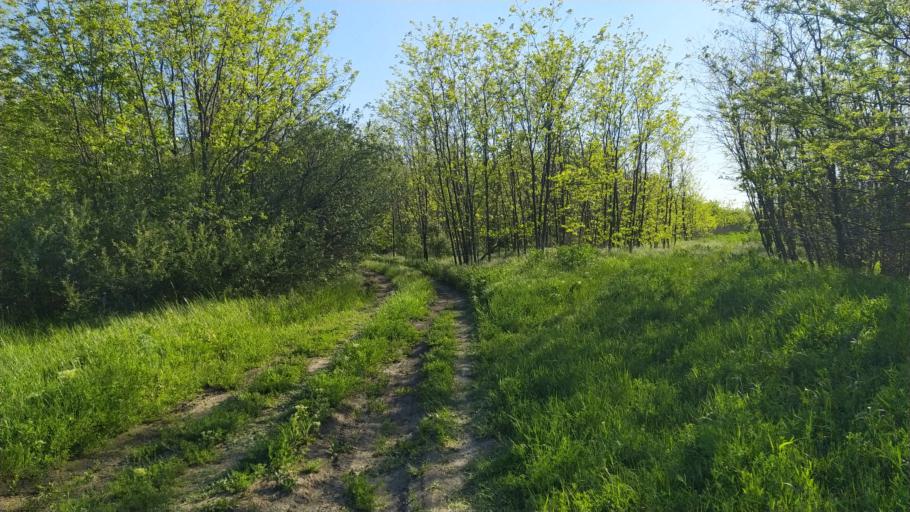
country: RU
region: Rostov
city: Bataysk
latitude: 47.0797
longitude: 39.7199
